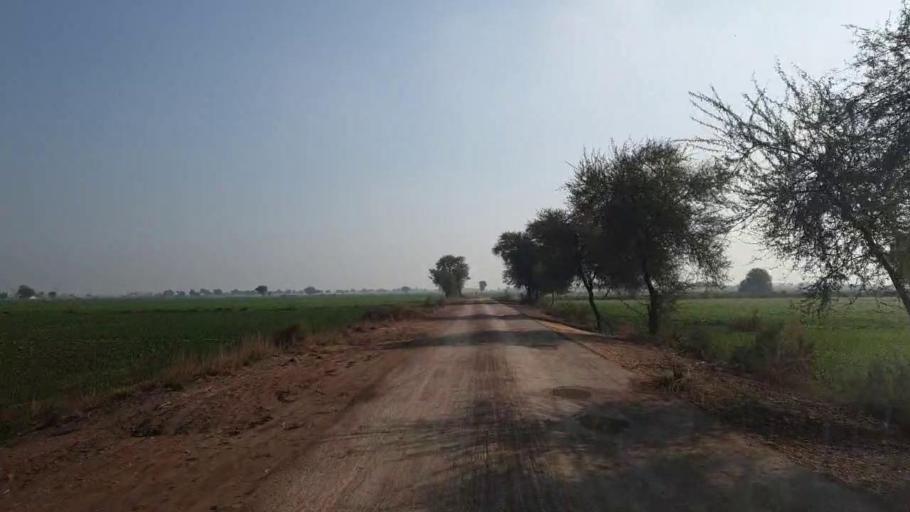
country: PK
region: Sindh
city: Shahdadpur
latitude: 25.9975
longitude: 68.6233
